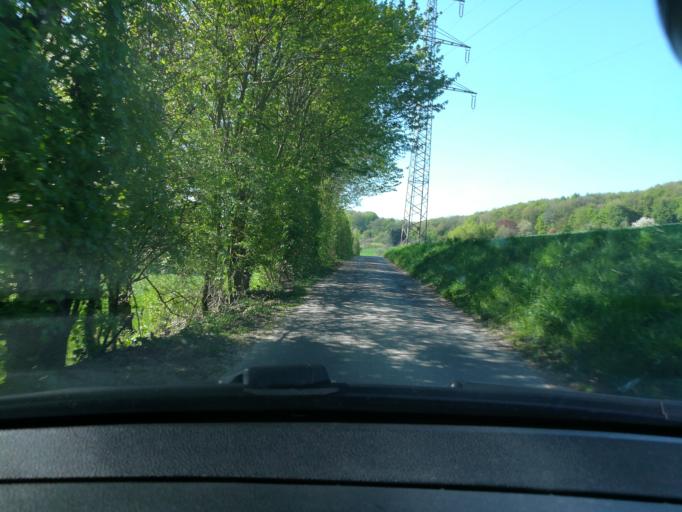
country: DE
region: North Rhine-Westphalia
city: Borgholzhausen
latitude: 52.1110
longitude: 8.3034
